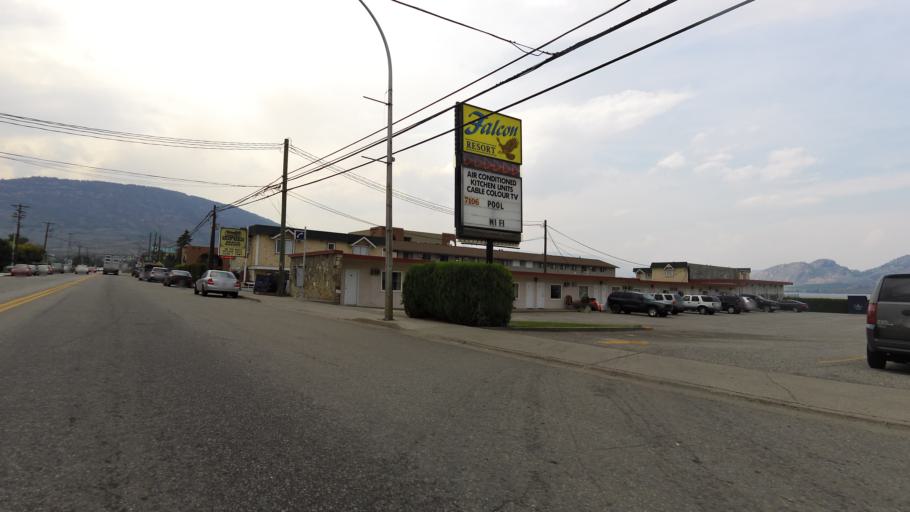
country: CA
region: British Columbia
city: Osoyoos
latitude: 49.0286
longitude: -119.4523
